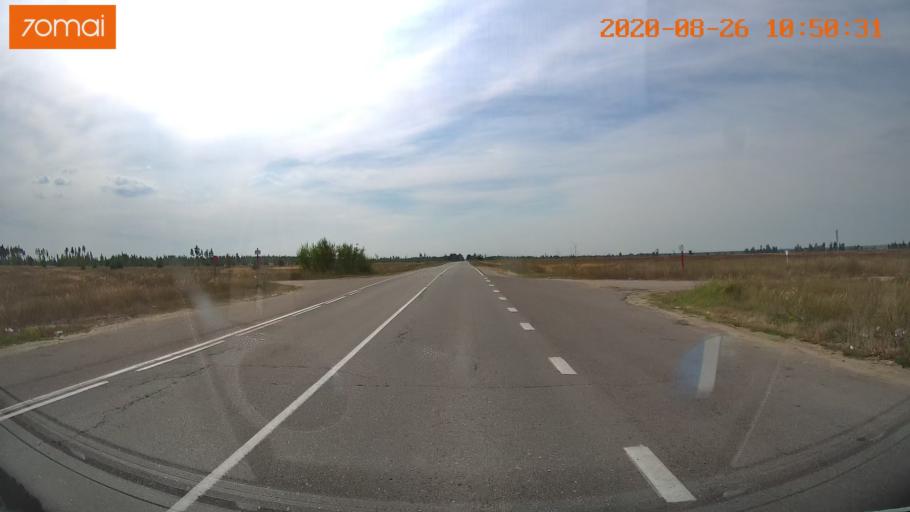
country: RU
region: Rjazan
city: Lashma
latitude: 54.6860
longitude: 41.1562
